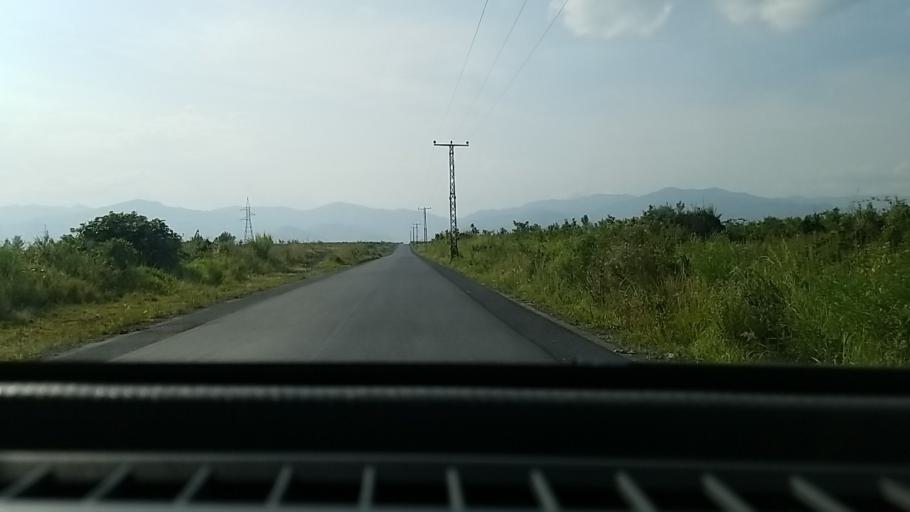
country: CD
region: Nord Kivu
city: Sake
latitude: -1.5966
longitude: 29.1067
